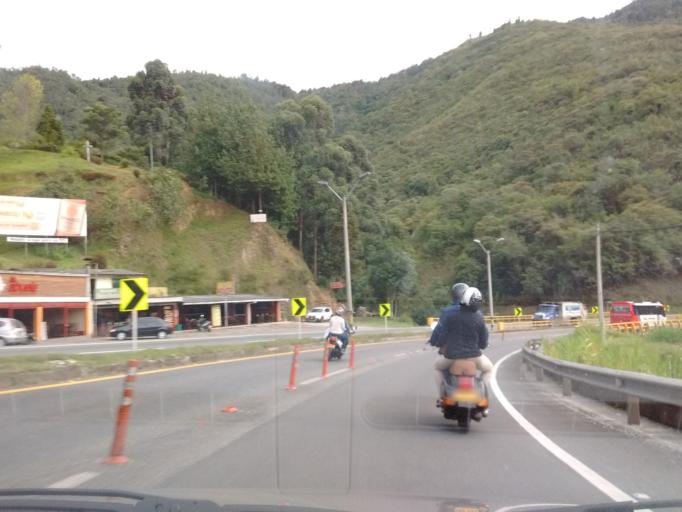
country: CO
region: Antioquia
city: Municipio de Copacabana
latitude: 6.3117
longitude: -75.5035
